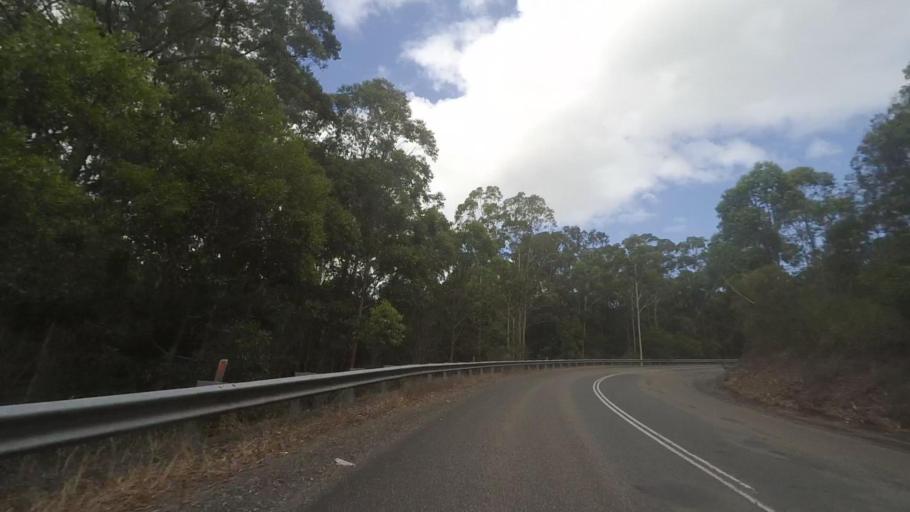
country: AU
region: New South Wales
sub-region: Great Lakes
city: Bulahdelah
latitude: -32.3882
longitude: 152.2415
